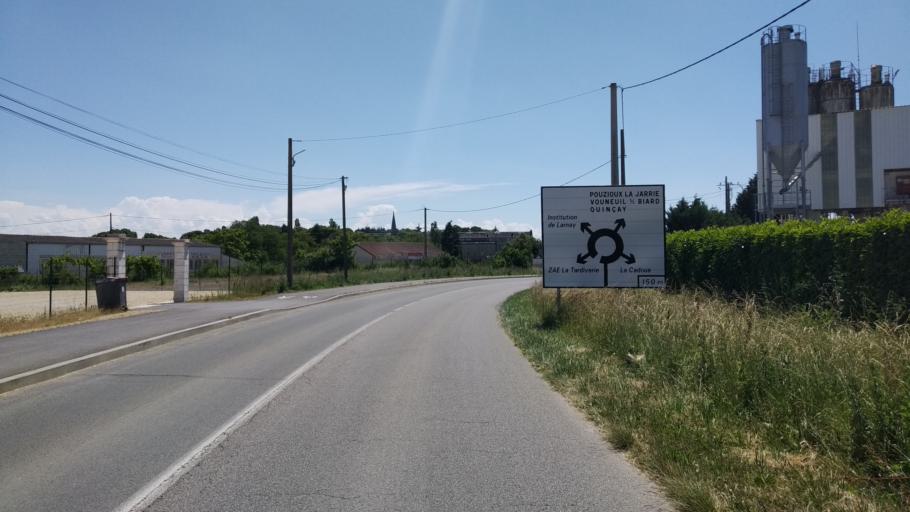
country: FR
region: Poitou-Charentes
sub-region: Departement de la Vienne
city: Biard
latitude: 46.5996
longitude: 0.3042
